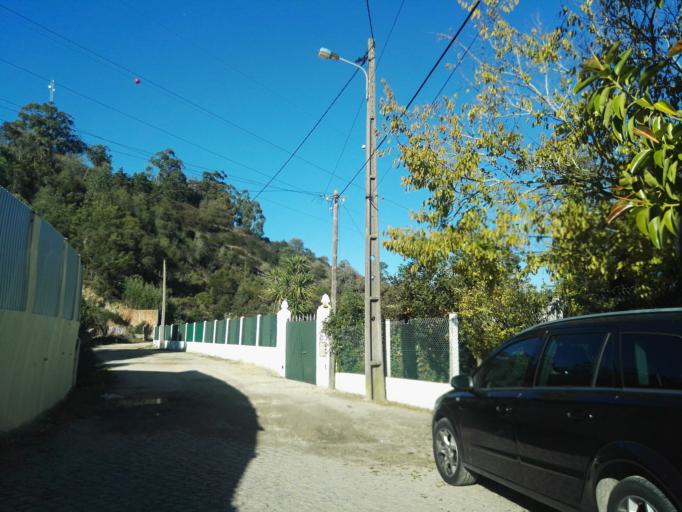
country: PT
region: Lisbon
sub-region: Mafra
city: Venda do Pinheiro
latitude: 38.9326
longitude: -9.2394
